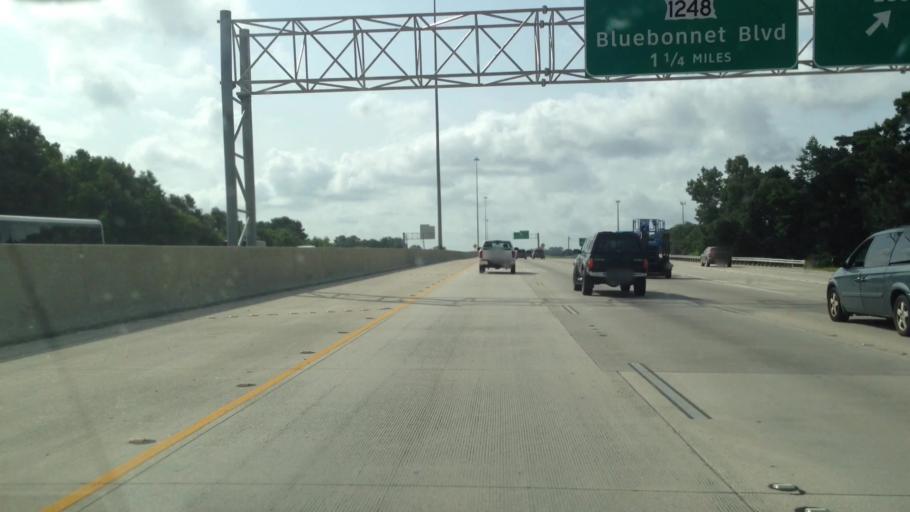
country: US
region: Louisiana
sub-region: East Baton Rouge Parish
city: Westminster
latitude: 30.4110
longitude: -91.1059
